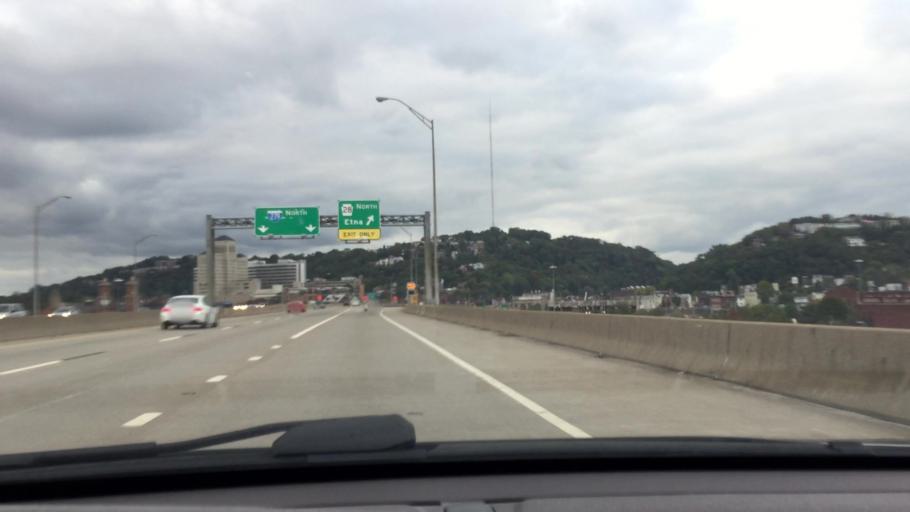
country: US
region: Pennsylvania
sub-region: Allegheny County
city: Pittsburgh
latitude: 40.4503
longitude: -79.9936
